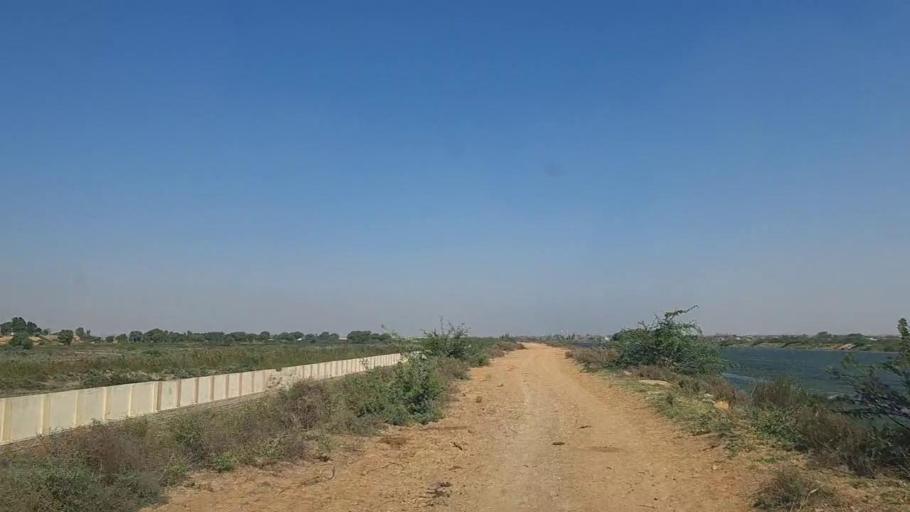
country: PK
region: Sindh
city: Thatta
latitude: 24.8142
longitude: 67.9878
